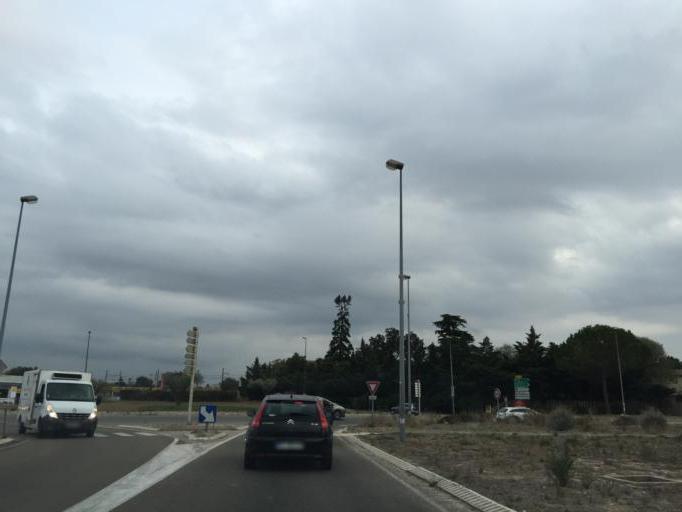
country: FR
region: Languedoc-Roussillon
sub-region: Departement du Gard
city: Remoulins
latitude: 43.9399
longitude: 4.5739
